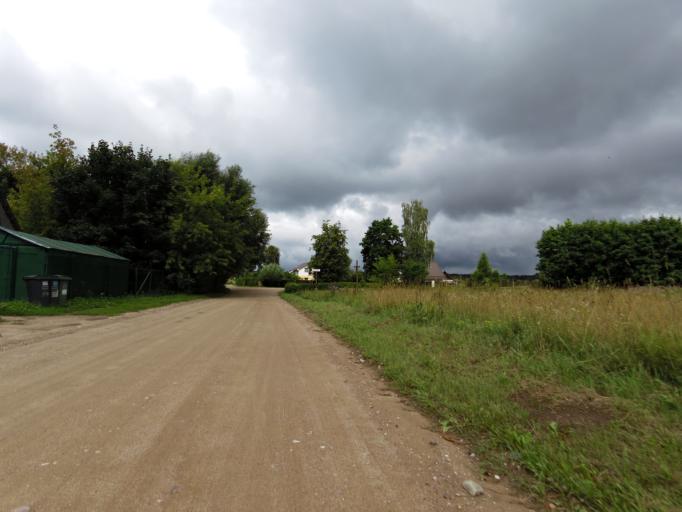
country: LT
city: Grigiskes
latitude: 54.7038
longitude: 25.1255
